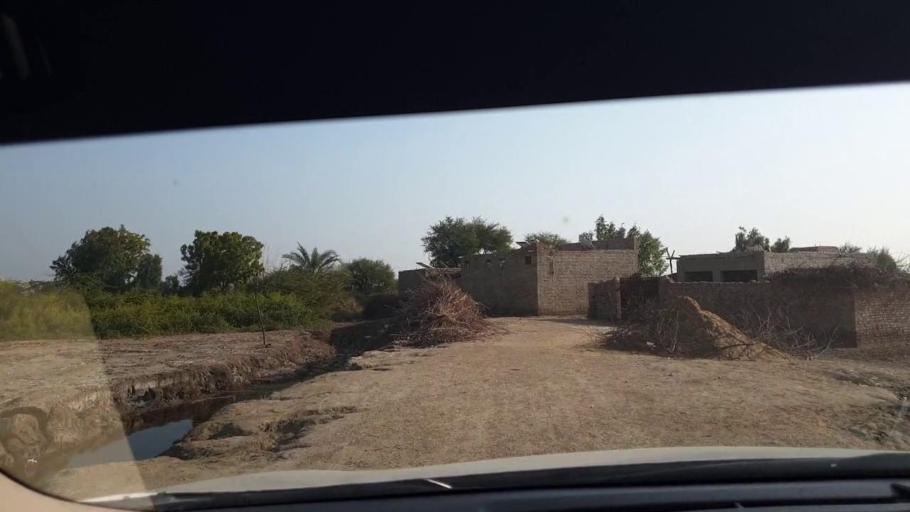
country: PK
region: Sindh
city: Berani
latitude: 25.8102
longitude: 68.7801
